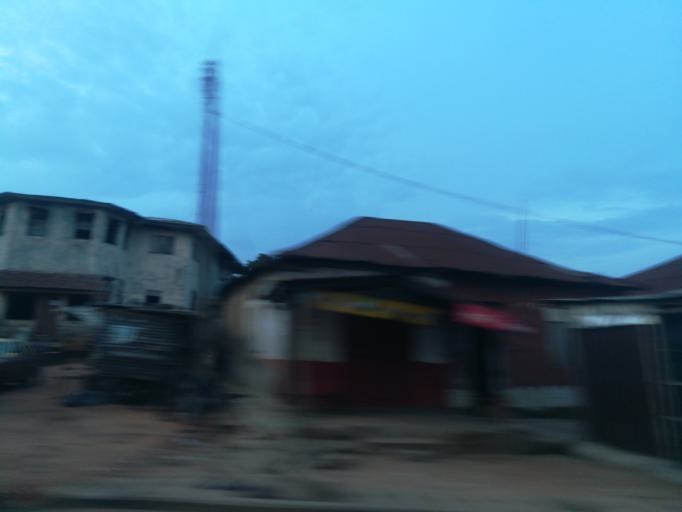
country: NG
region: Oyo
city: Ibadan
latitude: 7.3889
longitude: 3.9033
